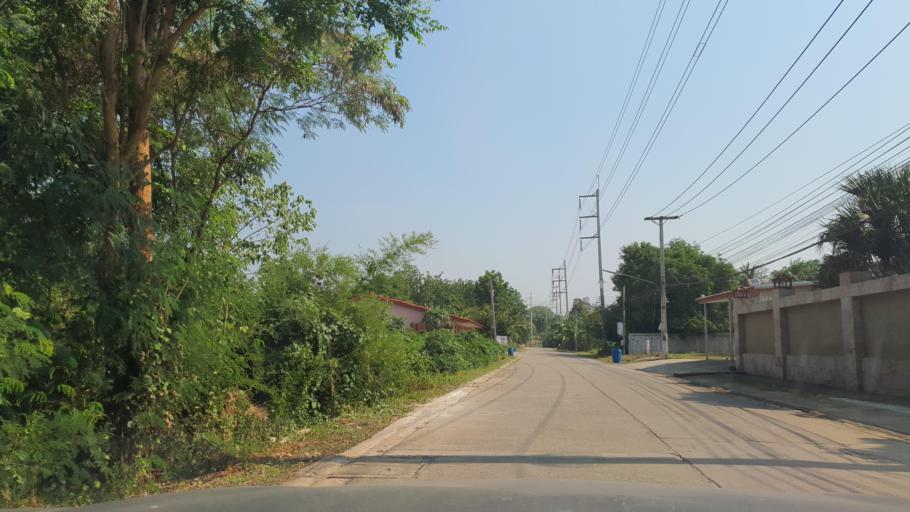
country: TH
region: Kanchanaburi
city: Kanchanaburi
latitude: 14.0656
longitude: 99.4857
